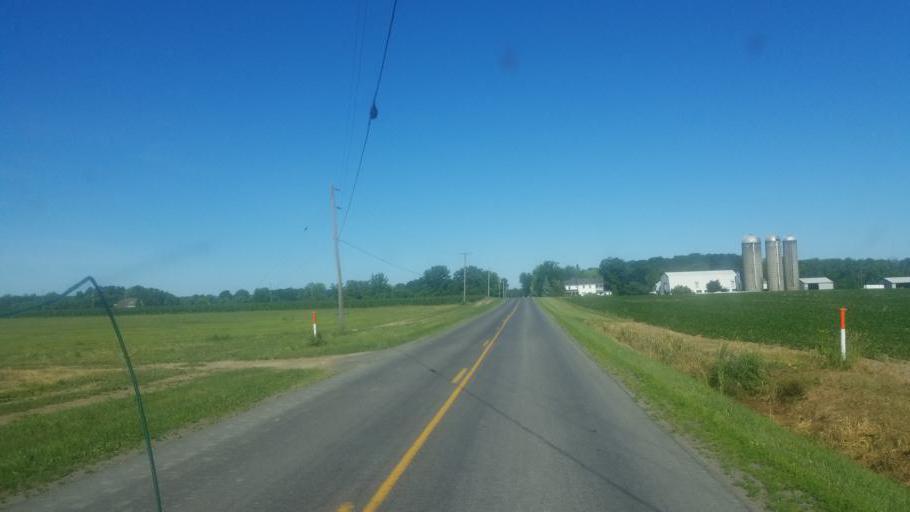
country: US
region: New York
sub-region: Ontario County
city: Canandaigua
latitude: 42.8360
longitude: -77.2039
